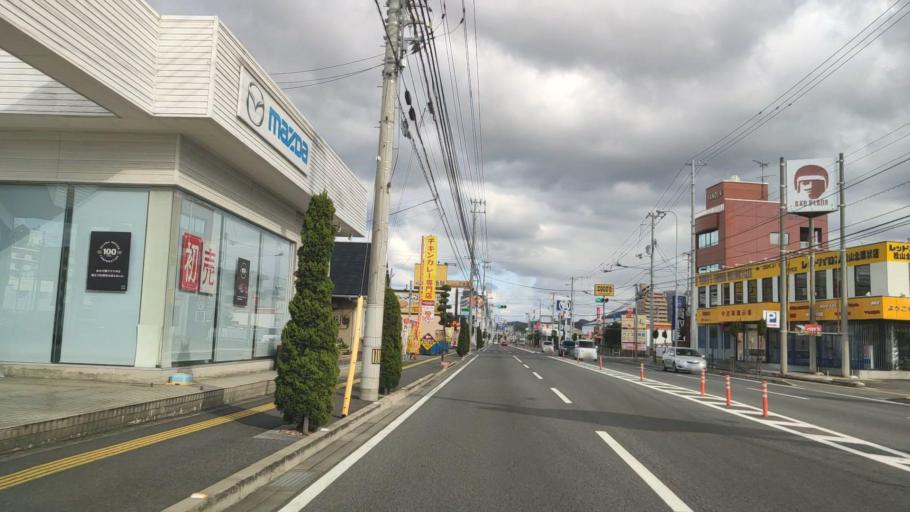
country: JP
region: Ehime
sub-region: Shikoku-chuo Shi
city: Matsuyama
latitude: 33.8583
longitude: 132.7487
